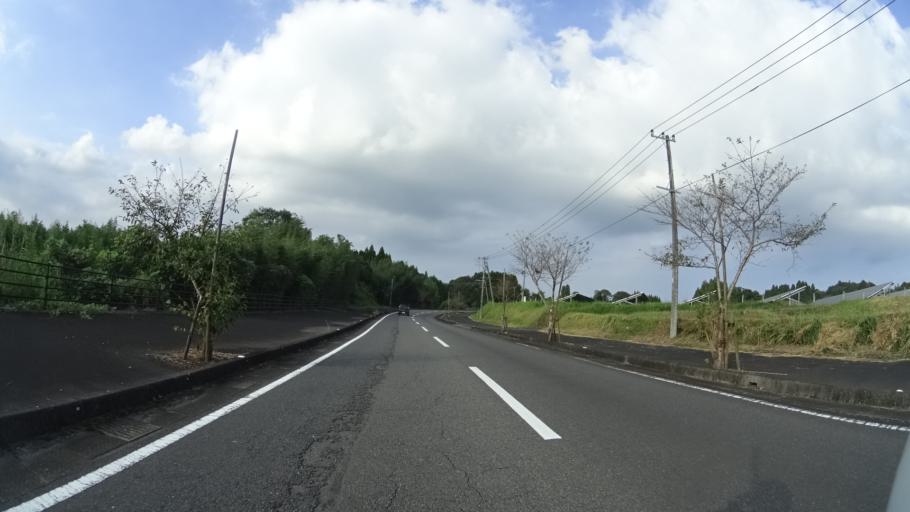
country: JP
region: Kagoshima
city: Okuchi-shinohara
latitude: 32.0177
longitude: 130.5838
